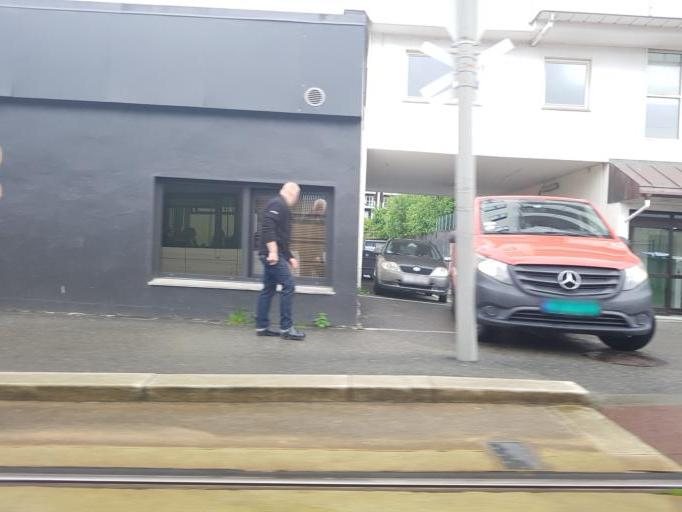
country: NO
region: Hordaland
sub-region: Bergen
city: Bergen
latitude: 60.3559
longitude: 5.3588
